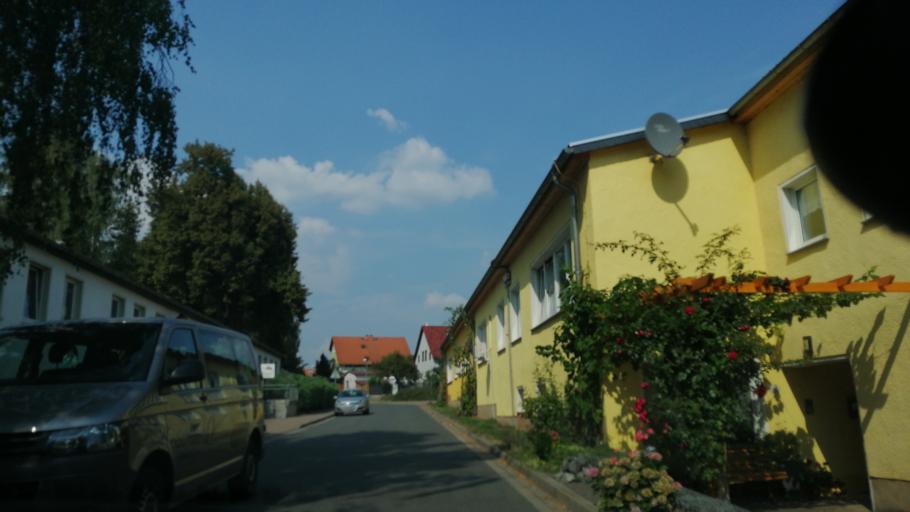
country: DE
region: Saxony-Anhalt
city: Riestedt
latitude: 51.4969
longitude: 11.3574
